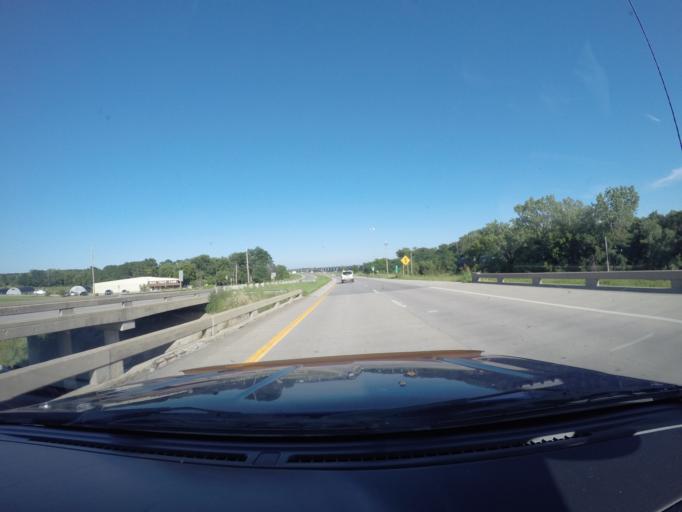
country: US
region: Kansas
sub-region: Shawnee County
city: Topeka
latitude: 39.0908
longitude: -95.5962
